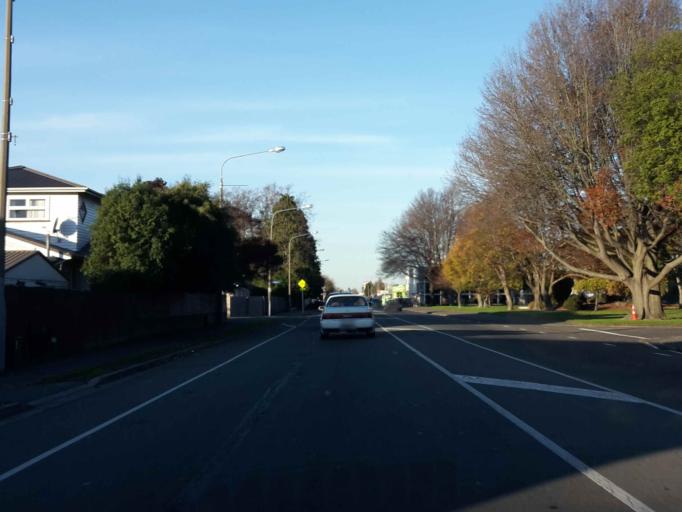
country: NZ
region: Canterbury
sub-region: Christchurch City
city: Christchurch
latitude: -43.5306
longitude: 172.5888
